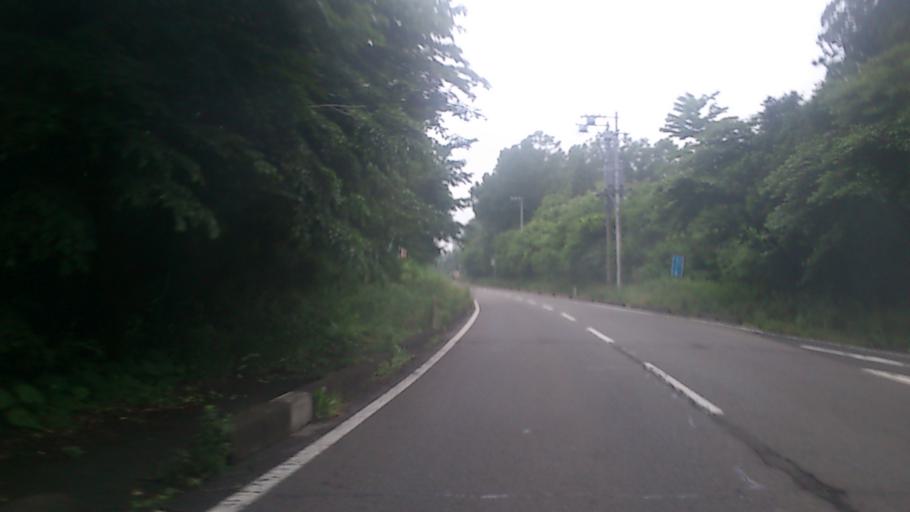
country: JP
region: Miyagi
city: Shiroishi
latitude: 38.1158
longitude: 140.5682
